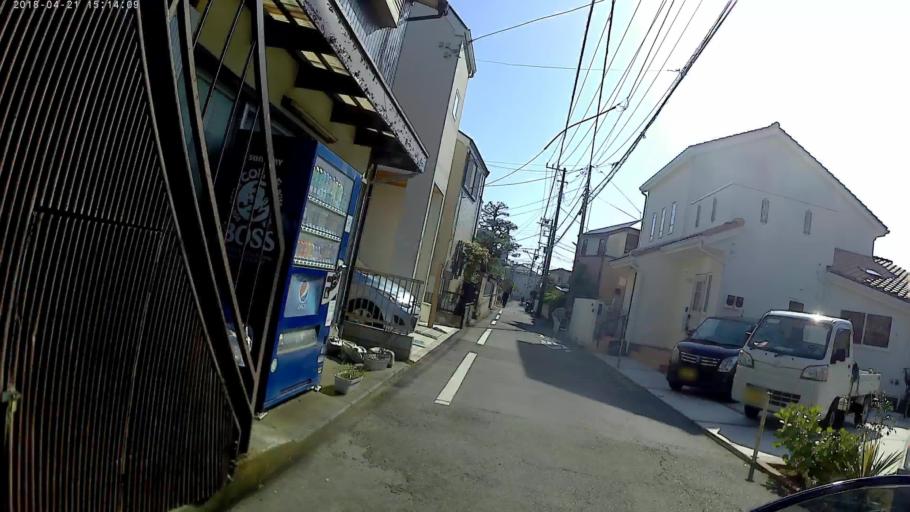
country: JP
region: Kanagawa
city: Fujisawa
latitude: 35.3199
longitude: 139.4665
